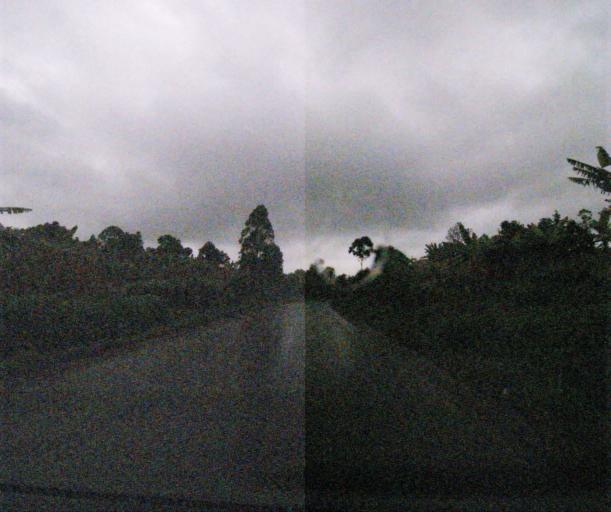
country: CM
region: West
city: Bansoa
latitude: 5.4762
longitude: 10.2829
